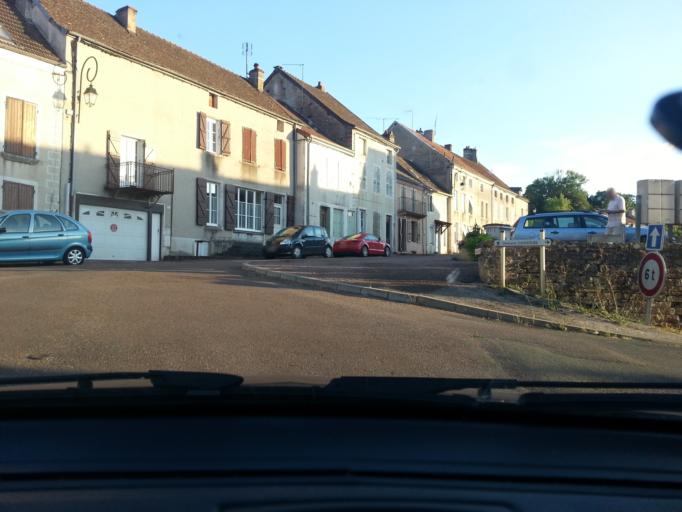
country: FR
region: Bourgogne
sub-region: Departement de Saone-et-Loire
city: Buxy
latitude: 46.7538
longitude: 4.7075
